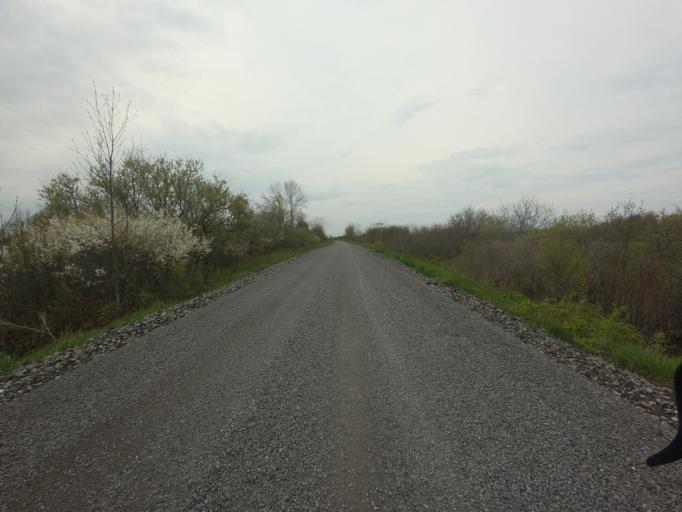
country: CA
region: Ontario
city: Carleton Place
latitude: 45.2026
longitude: -76.1688
